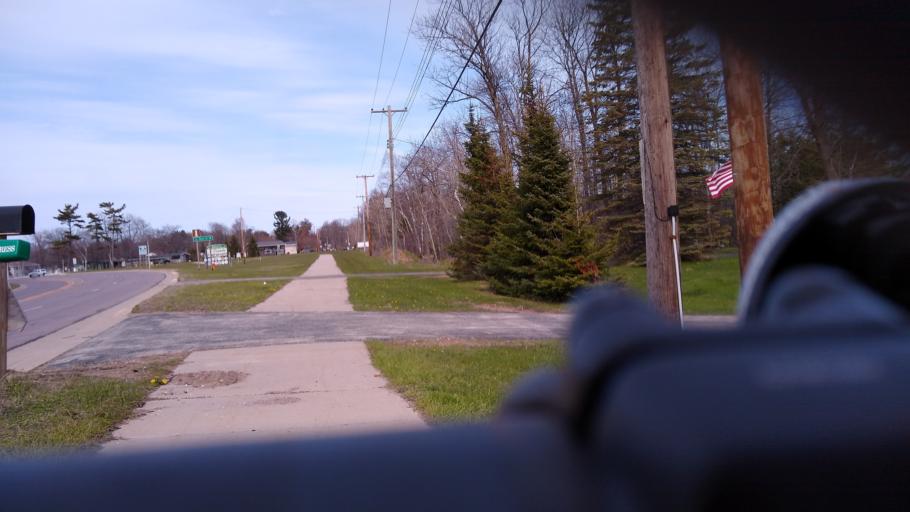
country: US
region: Michigan
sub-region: Delta County
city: Escanaba
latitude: 45.7145
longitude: -87.0833
